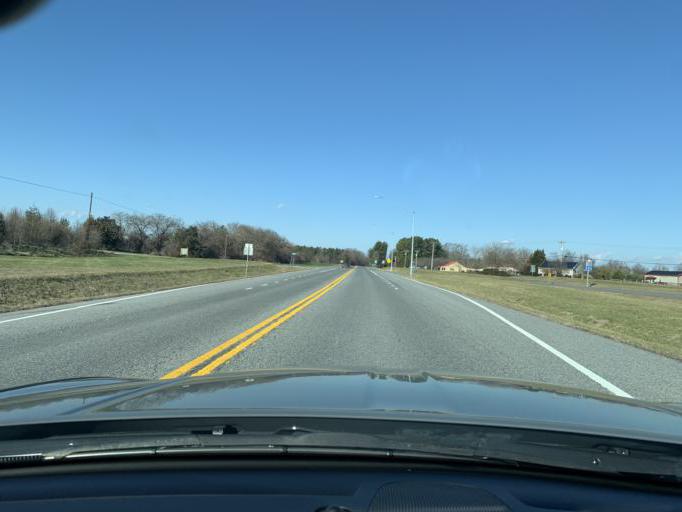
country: US
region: Maryland
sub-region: Queen Anne's County
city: Kingstown
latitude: 39.1536
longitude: -75.9810
